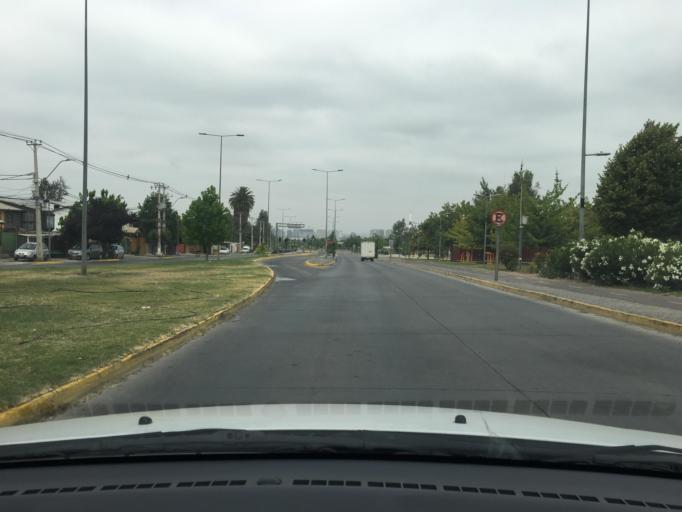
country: CL
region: Santiago Metropolitan
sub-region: Provincia de Santiago
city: Villa Presidente Frei, Nunoa, Santiago, Chile
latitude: -33.5114
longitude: -70.5616
